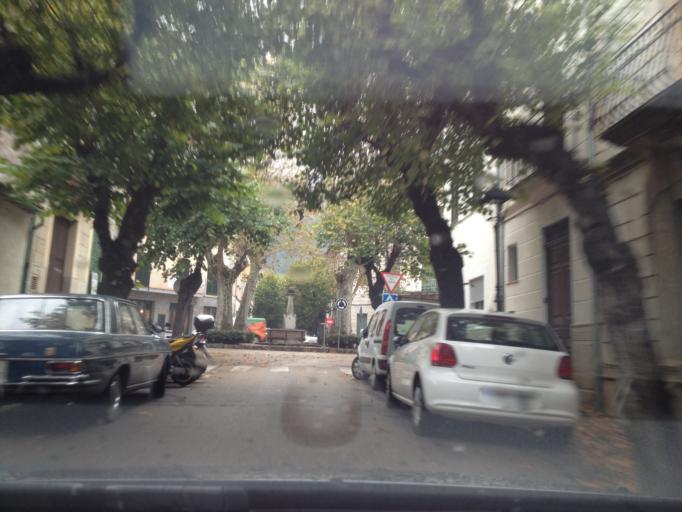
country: ES
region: Balearic Islands
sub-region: Illes Balears
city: Soller
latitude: 39.7687
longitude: 2.7111
